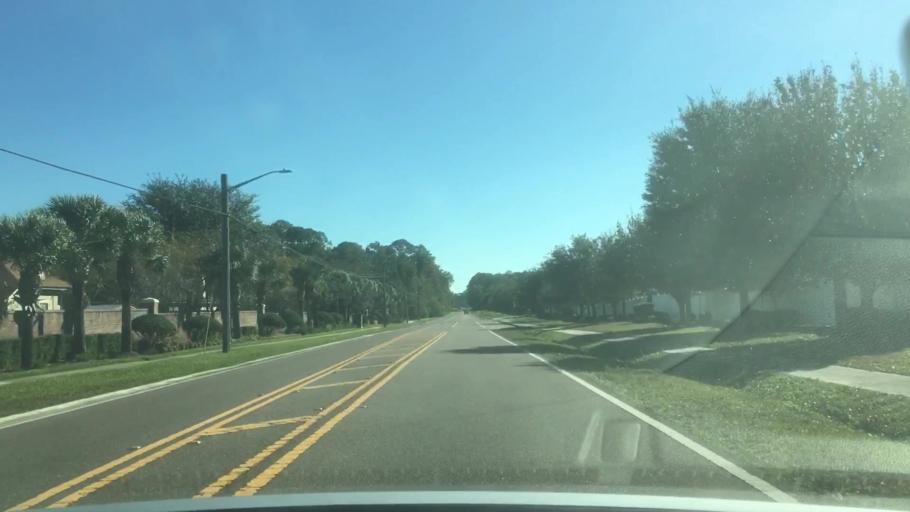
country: US
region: Florida
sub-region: Nassau County
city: Yulee
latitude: 30.4875
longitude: -81.6199
